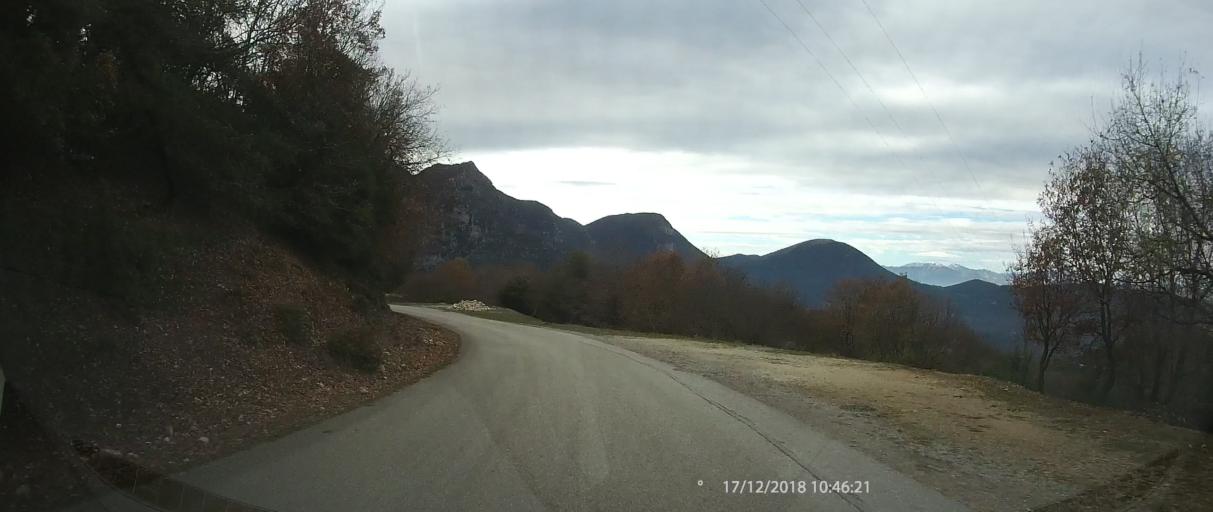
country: GR
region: Epirus
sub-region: Nomos Ioanninon
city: Konitsa
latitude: 39.9648
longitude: 20.7142
